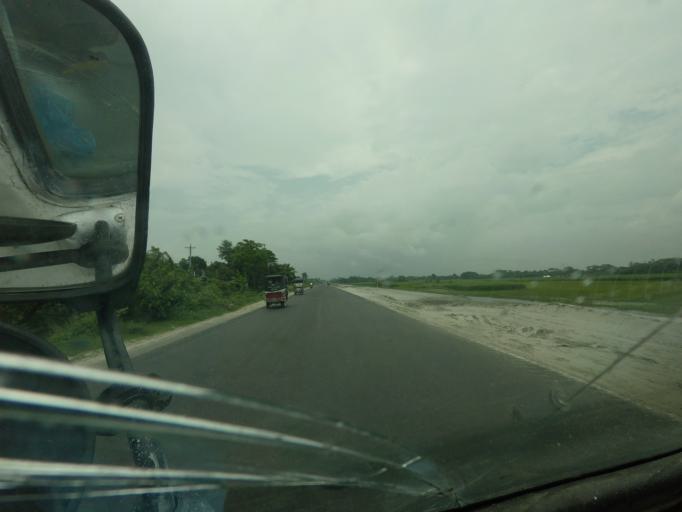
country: BD
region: Dhaka
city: Char Bhadrasan
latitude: 23.3788
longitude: 90.0107
